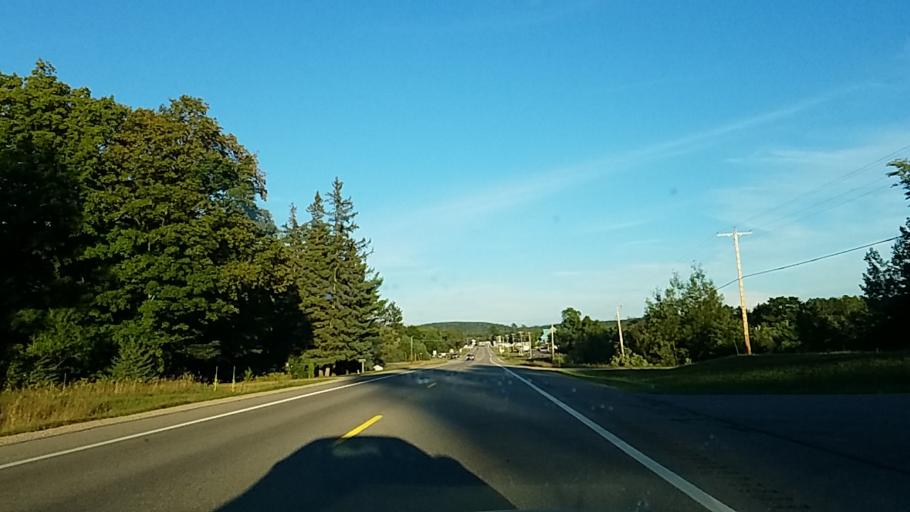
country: US
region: Michigan
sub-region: Alger County
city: Munising
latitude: 46.4392
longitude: -86.7141
